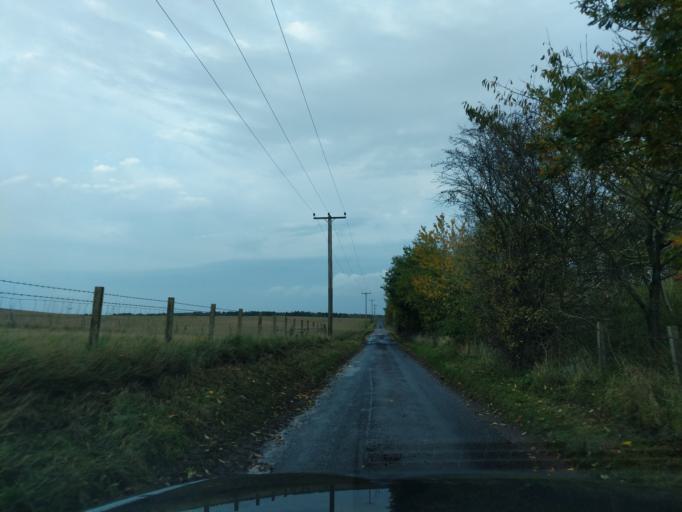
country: GB
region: Scotland
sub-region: Fife
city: Tayport
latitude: 56.4243
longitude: -2.8932
